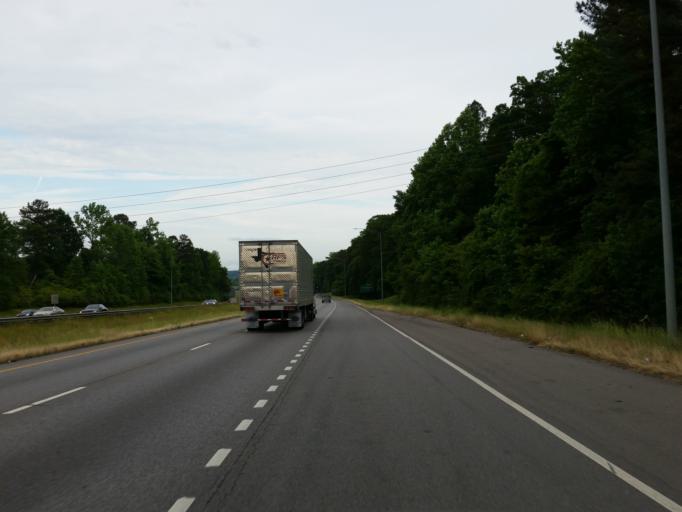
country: US
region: Alabama
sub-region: Tuscaloosa County
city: Holt
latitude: 33.1733
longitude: -87.4704
